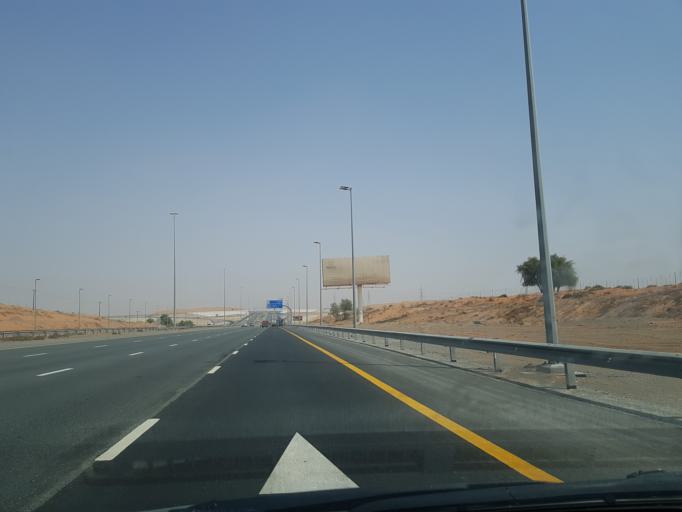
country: AE
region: Ra's al Khaymah
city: Ras al-Khaimah
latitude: 25.6316
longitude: 55.8223
